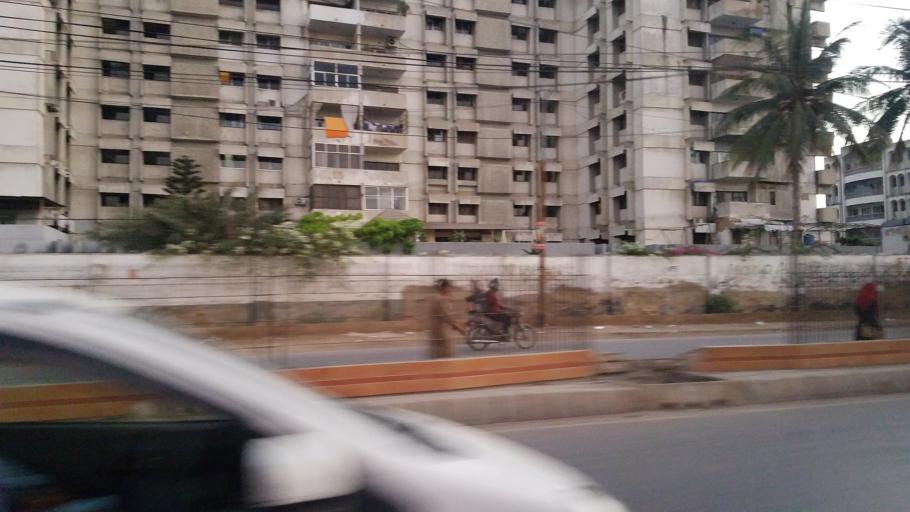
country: PK
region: Sindh
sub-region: Karachi District
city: Karachi
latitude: 24.8274
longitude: 67.0316
